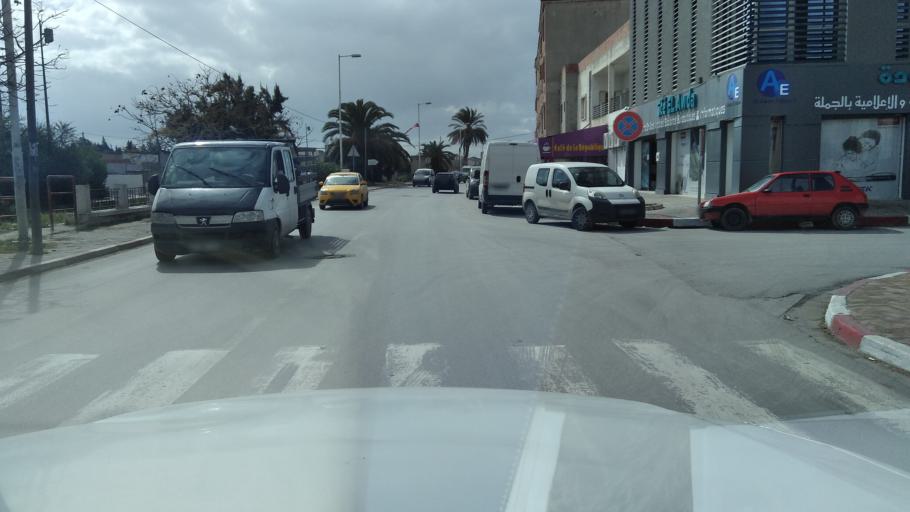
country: TN
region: Bin 'Arus
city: Ben Arous
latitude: 36.7481
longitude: 10.2255
